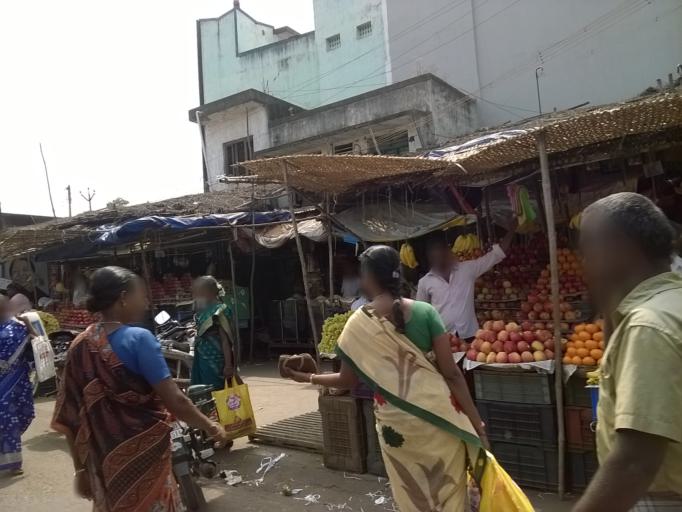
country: IN
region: Tamil Nadu
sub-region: Cuddalore
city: Panruti
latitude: 11.7732
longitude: 79.5511
